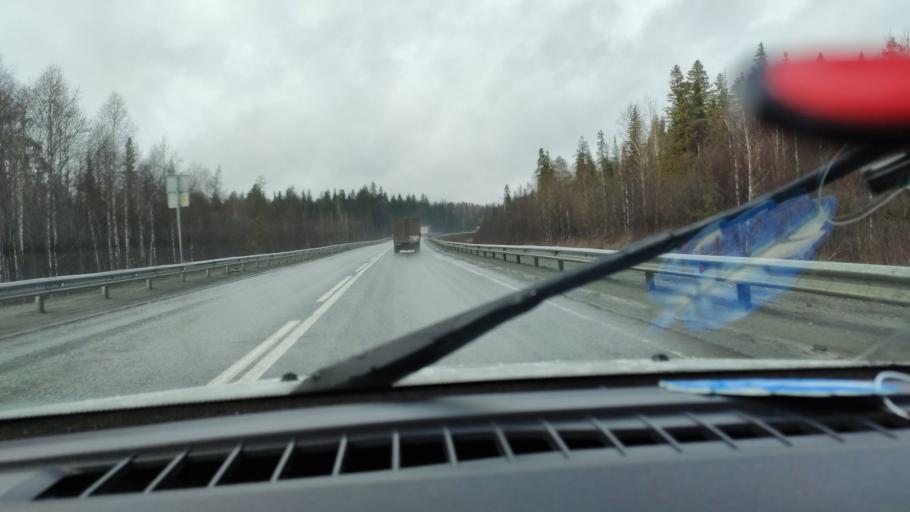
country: RU
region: Sverdlovsk
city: Bilimbay
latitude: 56.8530
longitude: 59.7803
